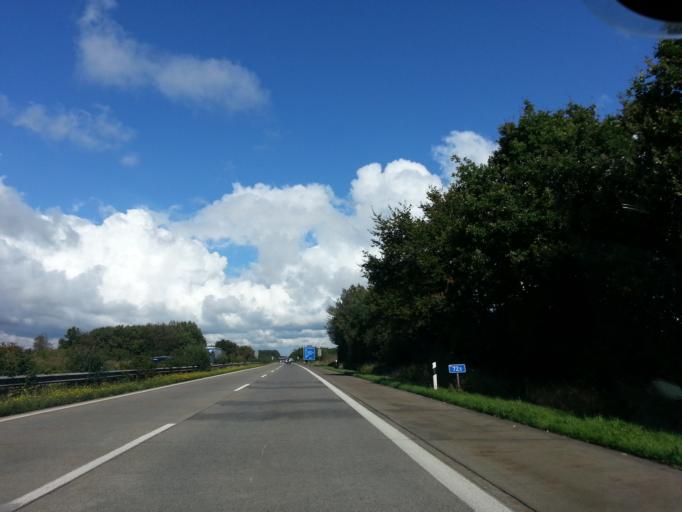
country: DE
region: Schleswig-Holstein
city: Scharbeutz
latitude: 53.9948
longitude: 10.7327
